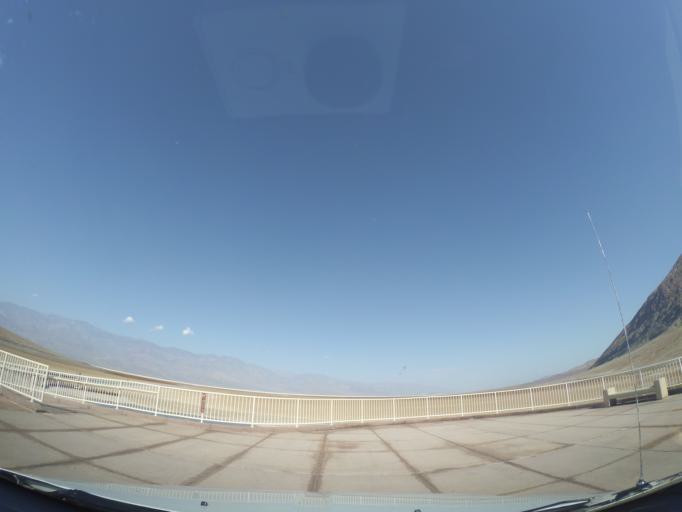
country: US
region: Nevada
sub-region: Nye County
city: Beatty
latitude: 36.2312
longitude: -116.7776
